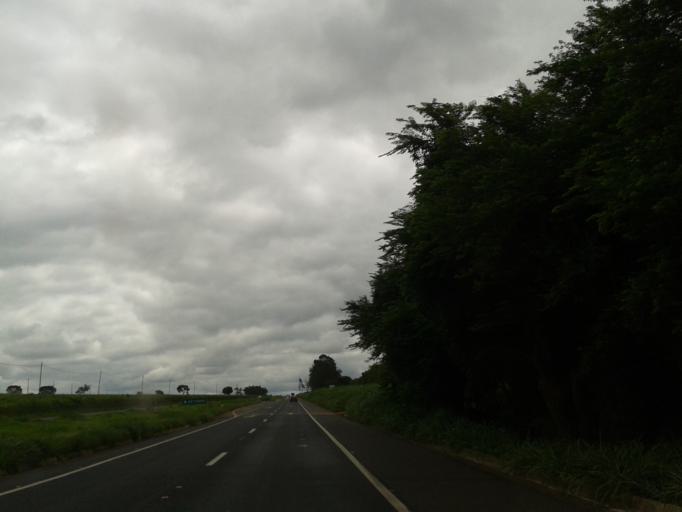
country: BR
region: Minas Gerais
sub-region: Uberlandia
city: Uberlandia
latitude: -18.8891
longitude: -48.4414
